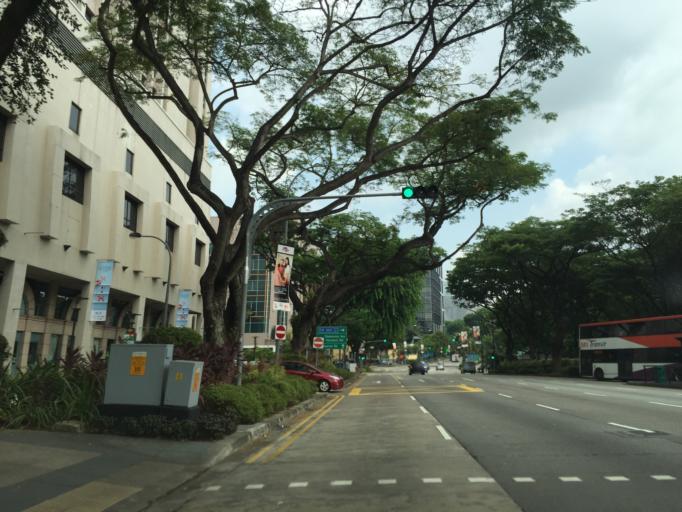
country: SG
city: Singapore
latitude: 1.2982
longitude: 103.8453
